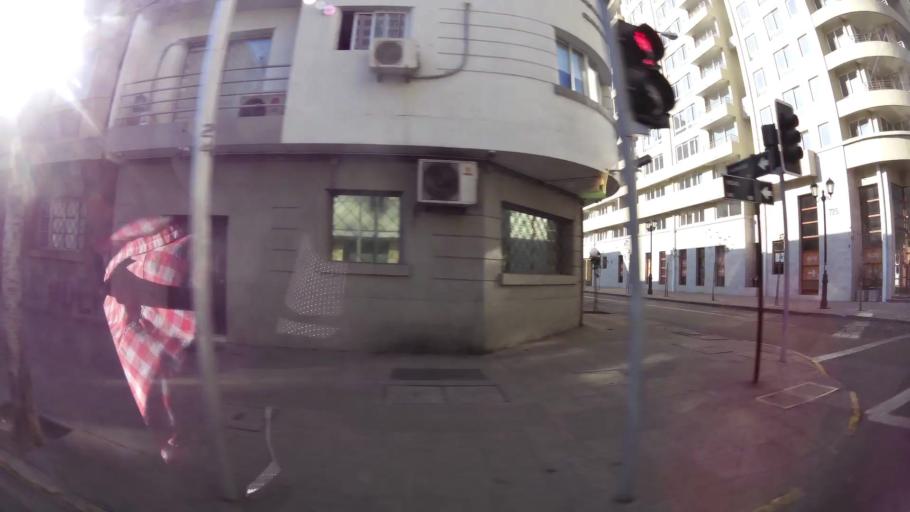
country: CL
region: Santiago Metropolitan
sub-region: Provincia de Santiago
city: Santiago
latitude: -33.4356
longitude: -70.6572
